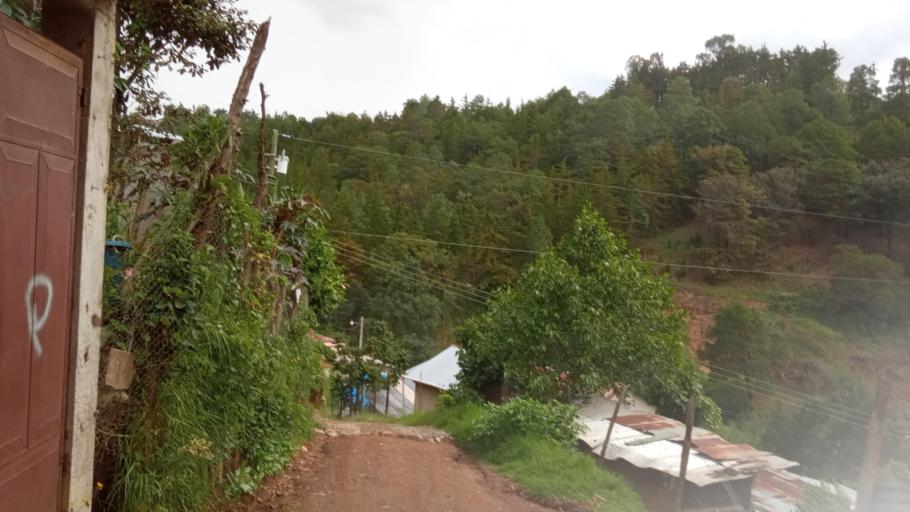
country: GT
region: San Marcos
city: Tejutla
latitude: 15.1183
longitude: -91.8035
